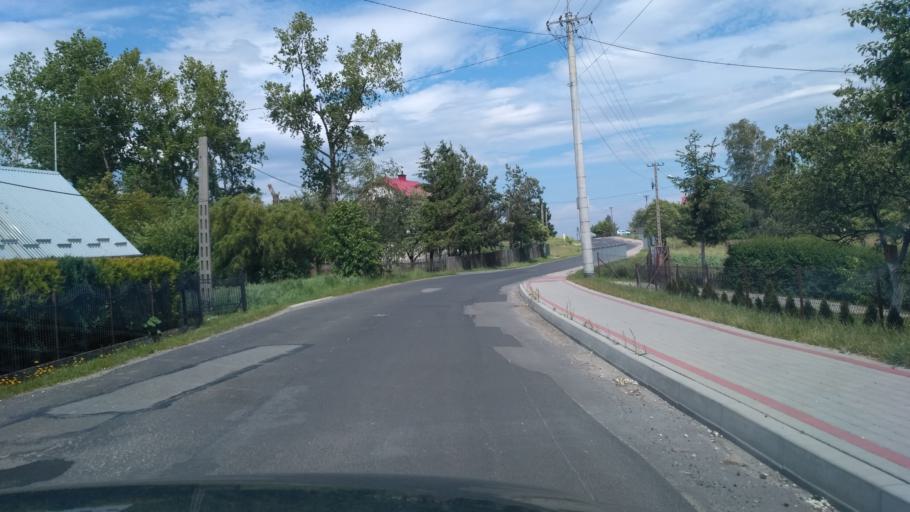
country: PL
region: Subcarpathian Voivodeship
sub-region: Powiat ropczycko-sedziszowski
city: Ropczyce
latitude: 50.0311
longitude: 21.6130
